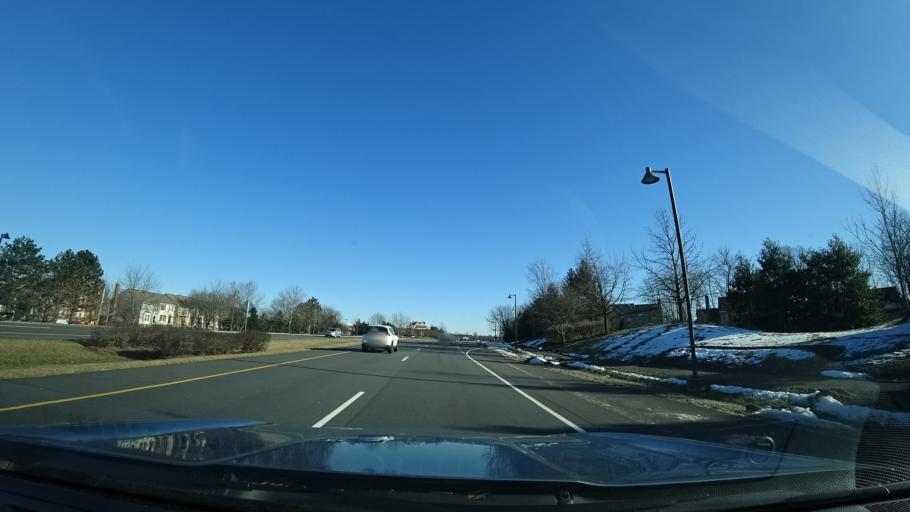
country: US
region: Virginia
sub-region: Loudoun County
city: Ashburn
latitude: 39.0452
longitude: -77.4798
